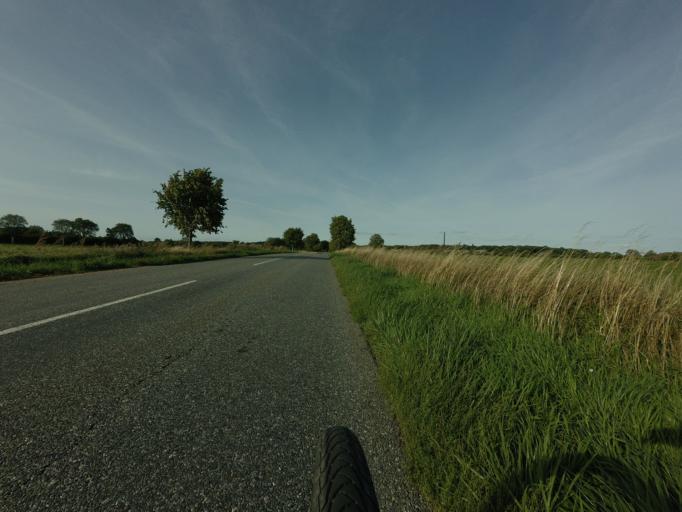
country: DK
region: Zealand
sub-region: Faxe Kommune
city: Fakse Ladeplads
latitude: 55.2489
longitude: 12.2216
